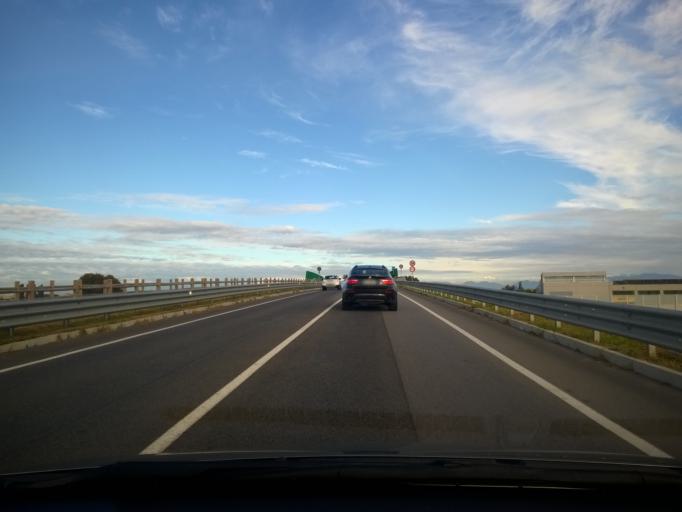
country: IT
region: Veneto
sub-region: Provincia di Venezia
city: Meolo
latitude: 45.6300
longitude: 12.4472
